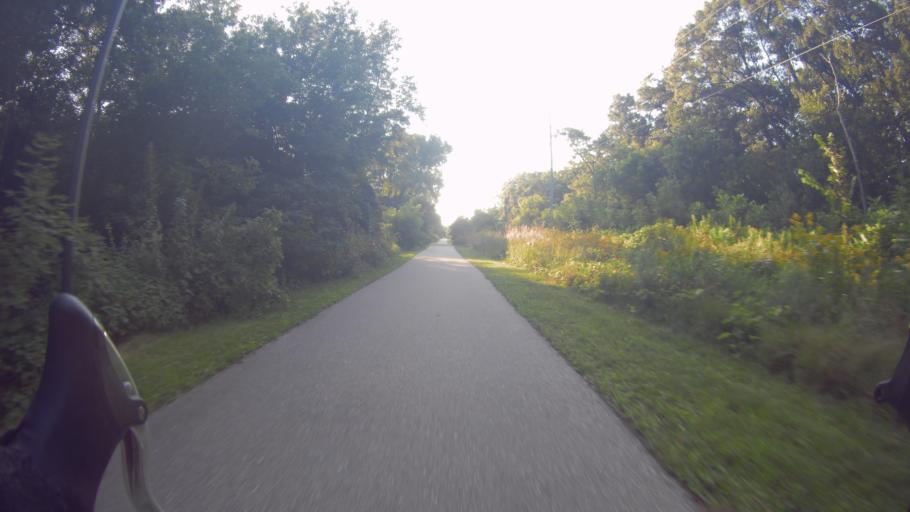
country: US
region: Wisconsin
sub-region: Dane County
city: Shorewood Hills
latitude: 43.0238
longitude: -89.4327
